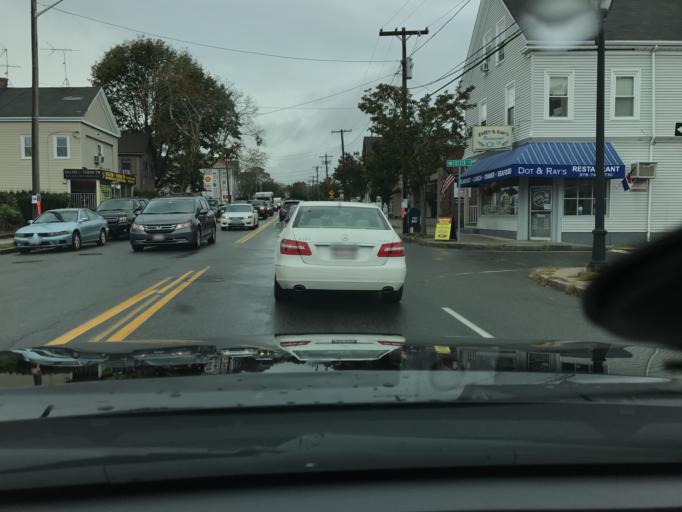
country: US
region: Massachusetts
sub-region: Essex County
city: Salem
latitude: 42.5263
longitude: -70.9007
